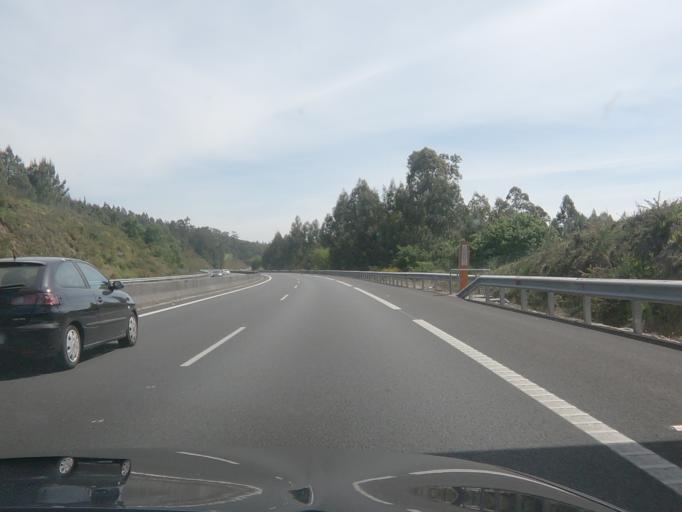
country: ES
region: Galicia
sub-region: Provincia de Pontevedra
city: Valga
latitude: 42.6941
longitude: -8.6355
